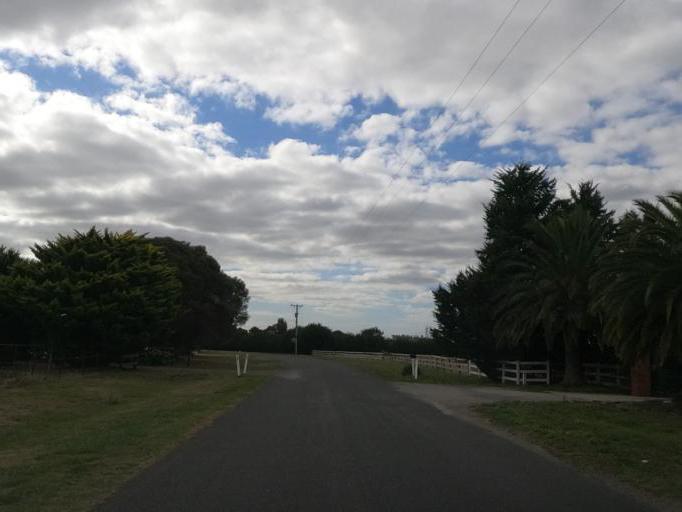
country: AU
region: Victoria
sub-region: Hume
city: Greenvale
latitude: -37.5559
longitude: 144.8705
